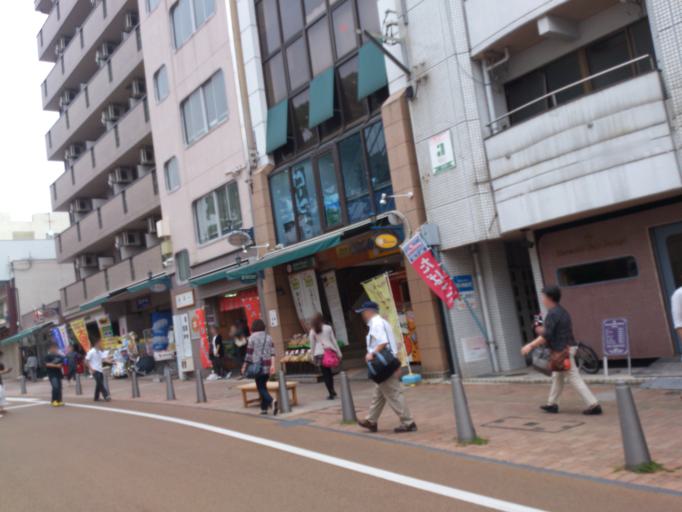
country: JP
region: Ehime
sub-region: Shikoku-chuo Shi
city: Matsuyama
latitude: 33.8442
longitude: 132.7718
